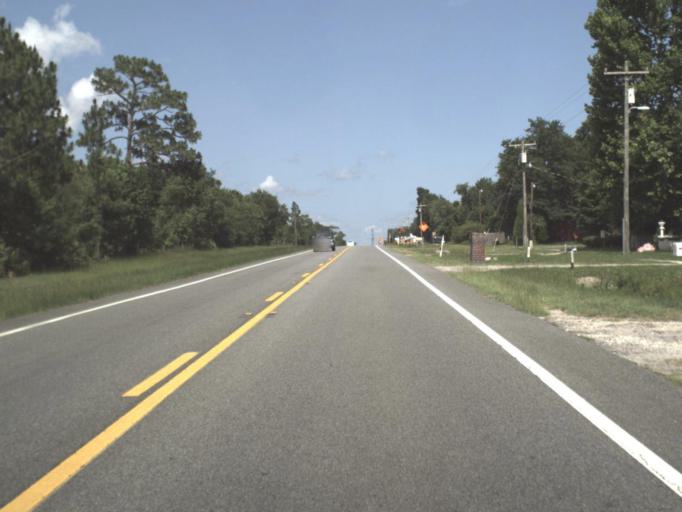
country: US
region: Florida
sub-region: Clay County
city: Asbury Lake
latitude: 29.9829
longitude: -81.7716
